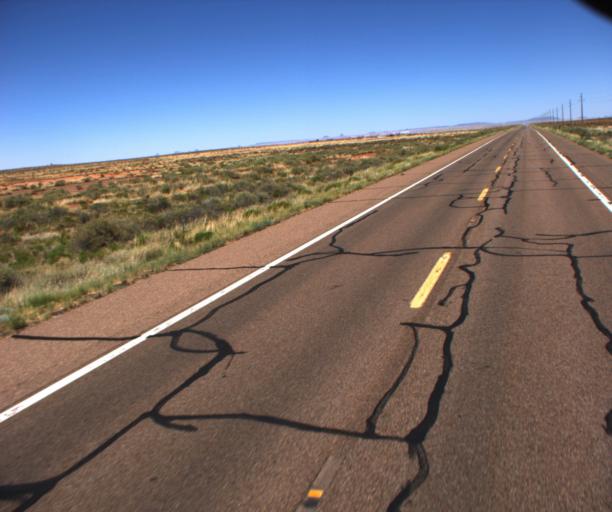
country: US
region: Arizona
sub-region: Coconino County
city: LeChee
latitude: 34.9551
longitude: -110.7540
